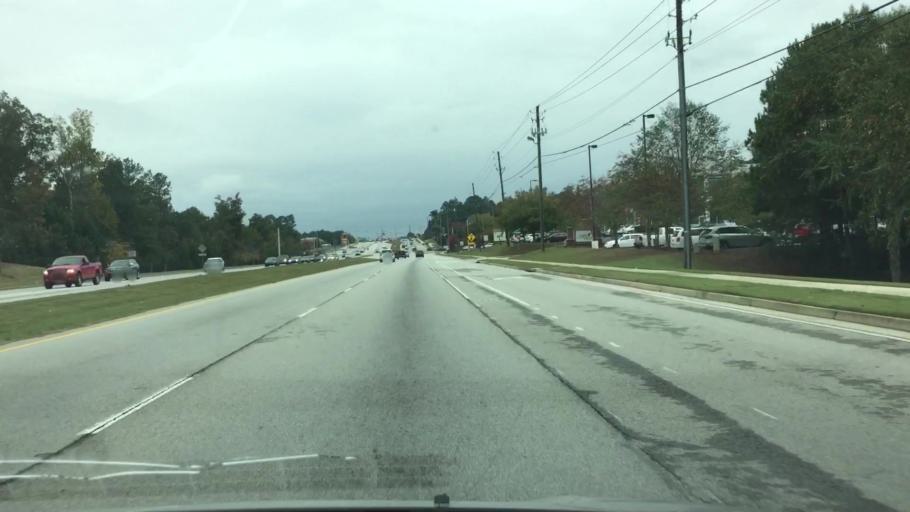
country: US
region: Georgia
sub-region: Henry County
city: Stockbridge
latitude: 33.5134
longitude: -84.2139
